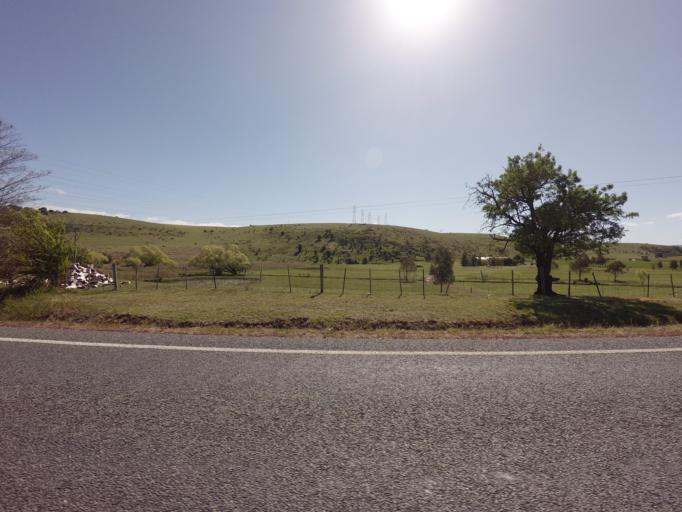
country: AU
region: Tasmania
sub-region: Derwent Valley
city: New Norfolk
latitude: -42.6629
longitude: 146.9336
